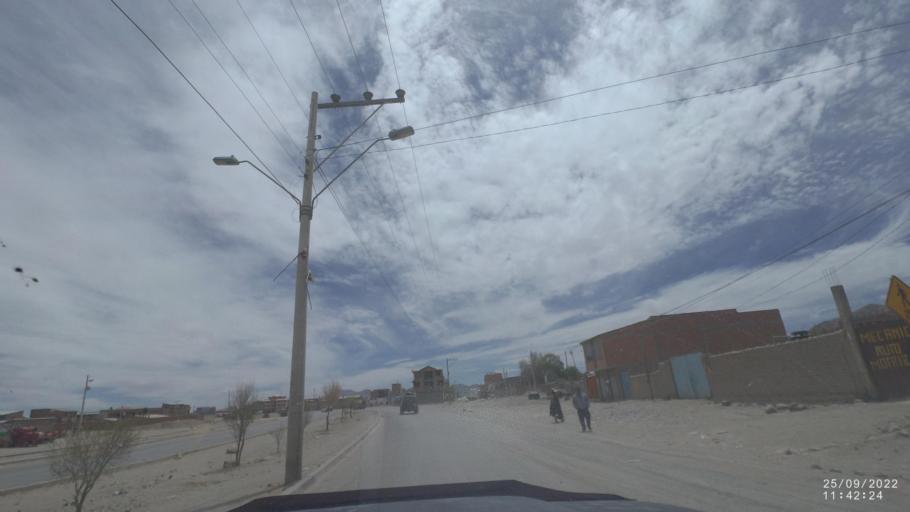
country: BO
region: Oruro
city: Challapata
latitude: -18.8973
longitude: -66.7765
